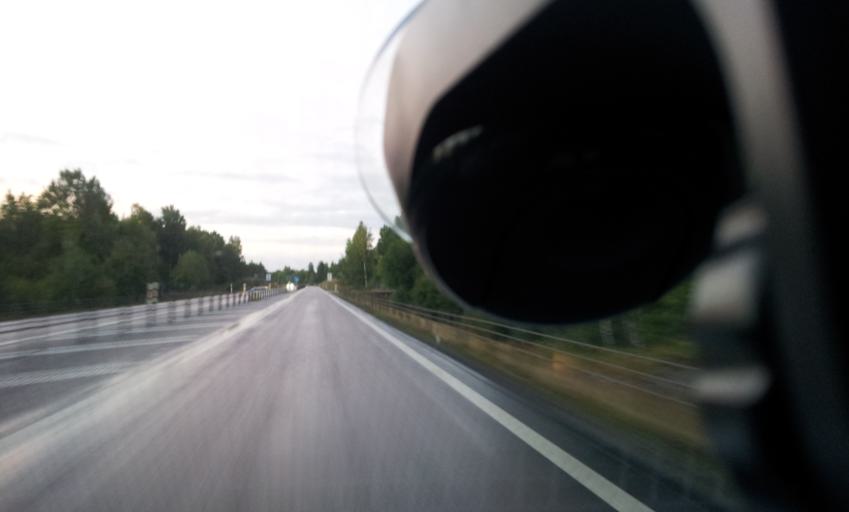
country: SE
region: Kalmar
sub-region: Oskarshamns Kommun
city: Oskarshamn
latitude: 57.2220
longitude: 16.4361
